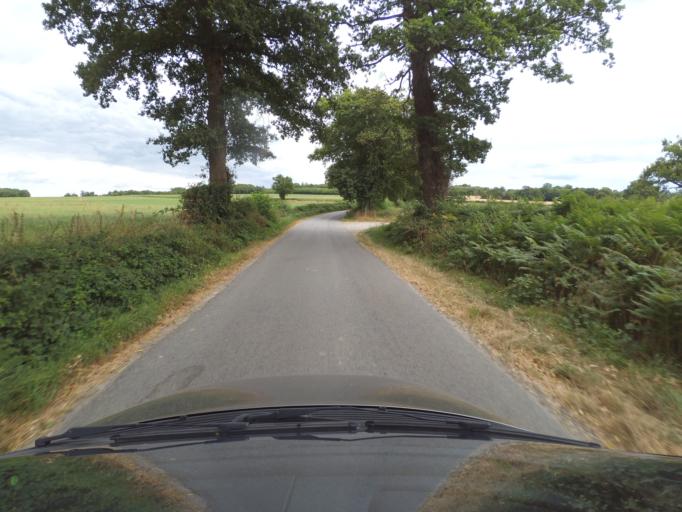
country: FR
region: Limousin
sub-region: Departement de la Haute-Vienne
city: Arnac-la-Poste
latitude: 46.2384
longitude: 1.3547
